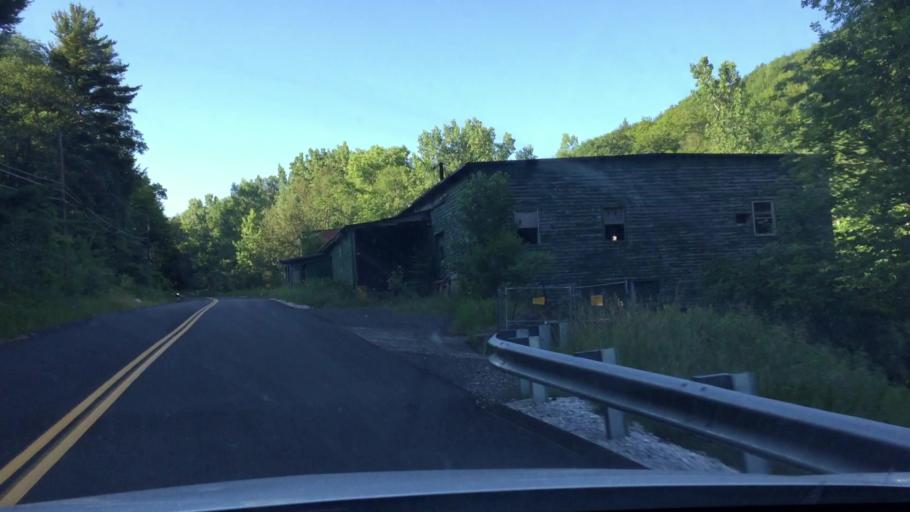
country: US
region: Massachusetts
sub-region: Berkshire County
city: Lee
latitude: 42.2888
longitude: -73.2149
